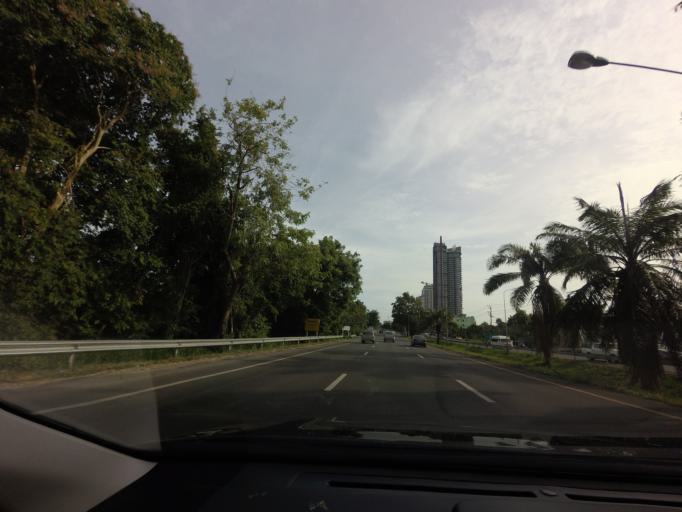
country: TH
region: Chon Buri
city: Si Racha
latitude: 13.1962
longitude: 100.9374
